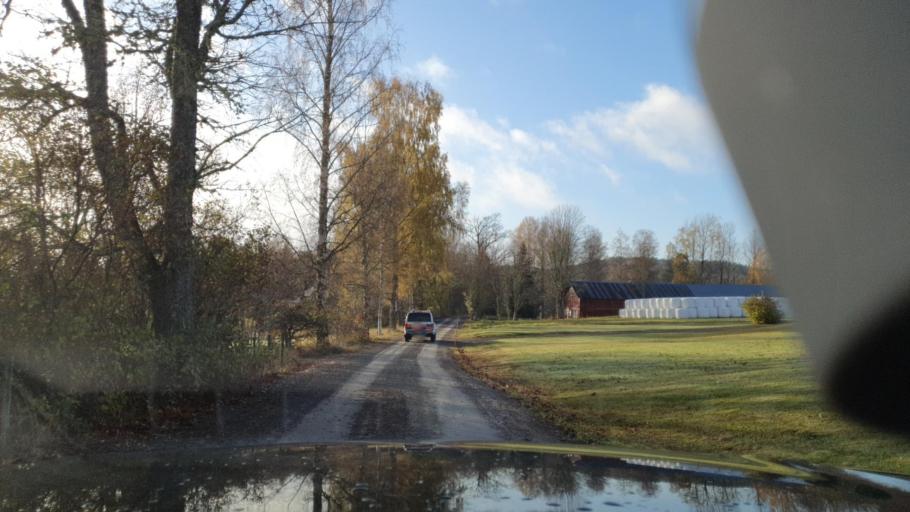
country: SE
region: Vaermland
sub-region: Grums Kommun
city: Grums
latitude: 59.4866
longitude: 12.9349
